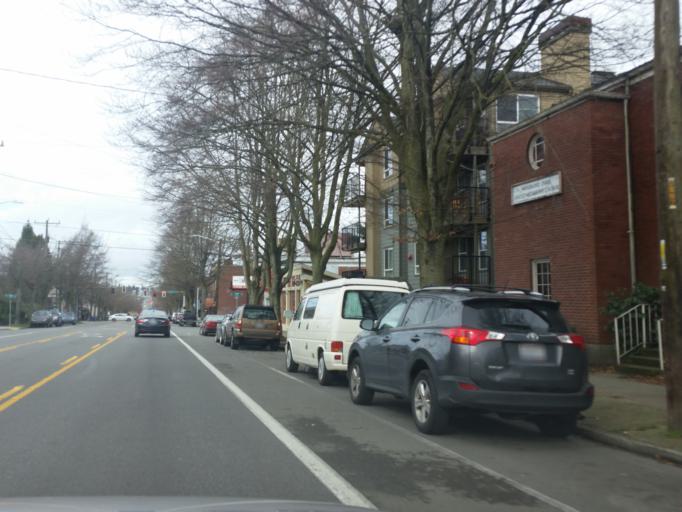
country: US
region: Washington
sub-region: King County
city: Shoreline
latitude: 47.6856
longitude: -122.3553
